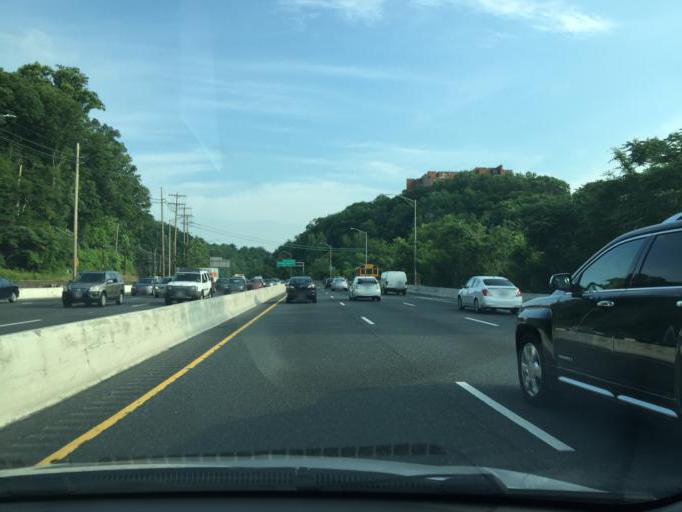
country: US
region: Maryland
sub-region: Baltimore County
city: Towson
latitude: 39.3528
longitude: -76.6473
